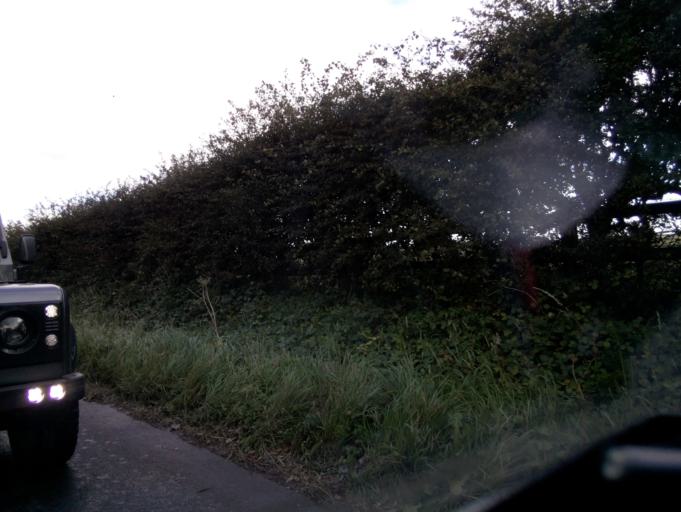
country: GB
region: England
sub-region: Devon
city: Kingsbridge
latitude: 50.3042
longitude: -3.7868
